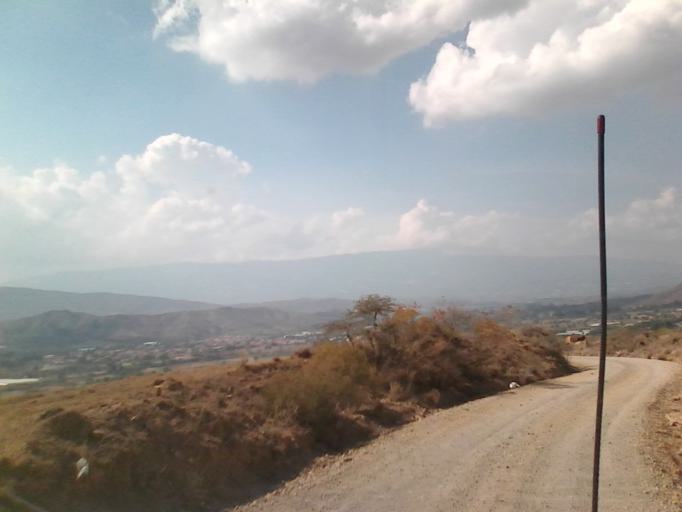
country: CO
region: Boyaca
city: Sachica
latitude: 5.5758
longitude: -73.5264
